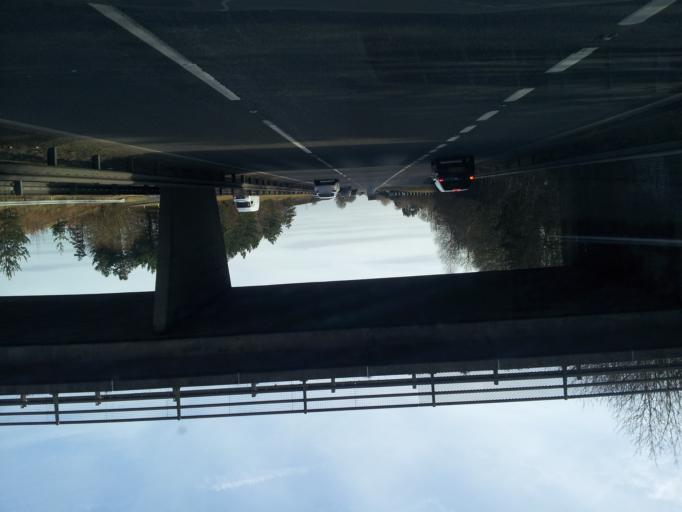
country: GB
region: England
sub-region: Cambridgeshire
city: Eaton Socon
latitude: 52.2370
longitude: -0.2834
